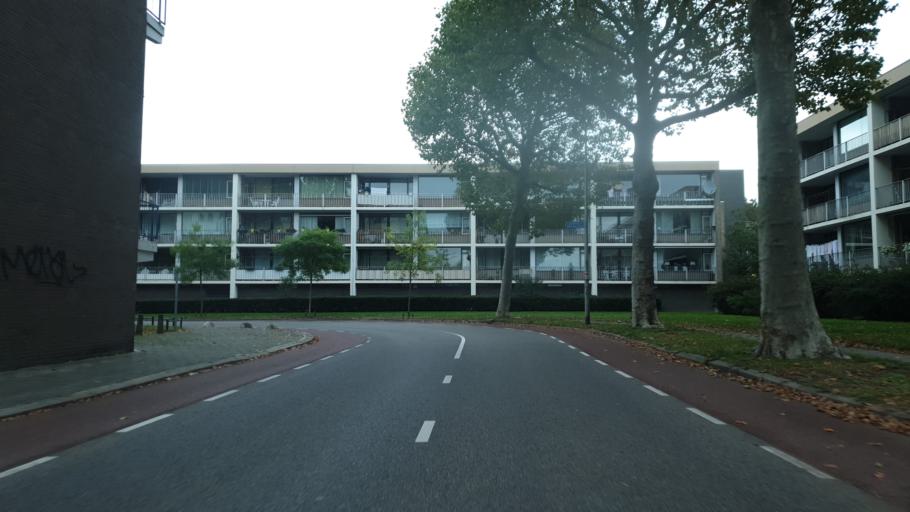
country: NL
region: Gelderland
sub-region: Gemeente Nijmegen
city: Lindenholt
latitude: 51.8156
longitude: 5.8088
